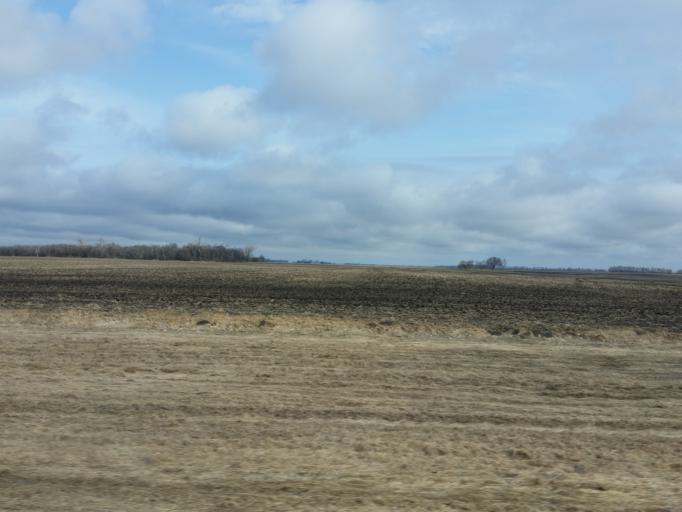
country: US
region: North Dakota
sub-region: Traill County
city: Hillsboro
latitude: 47.4978
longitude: -97.1468
